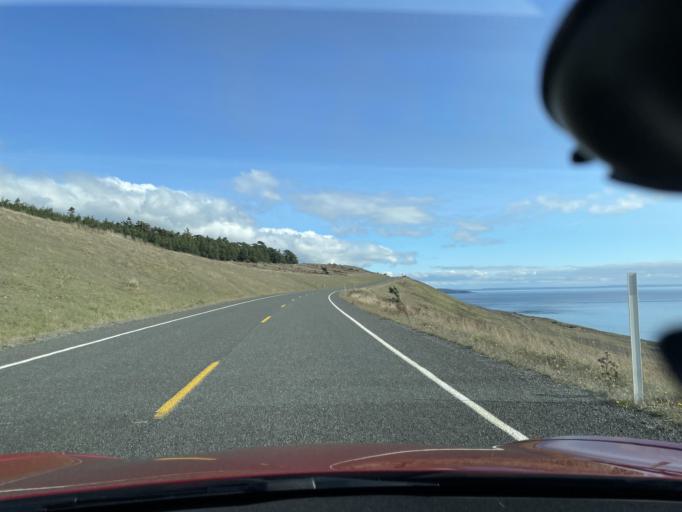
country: US
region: Washington
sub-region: San Juan County
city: Friday Harbor
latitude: 48.4570
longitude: -122.9820
